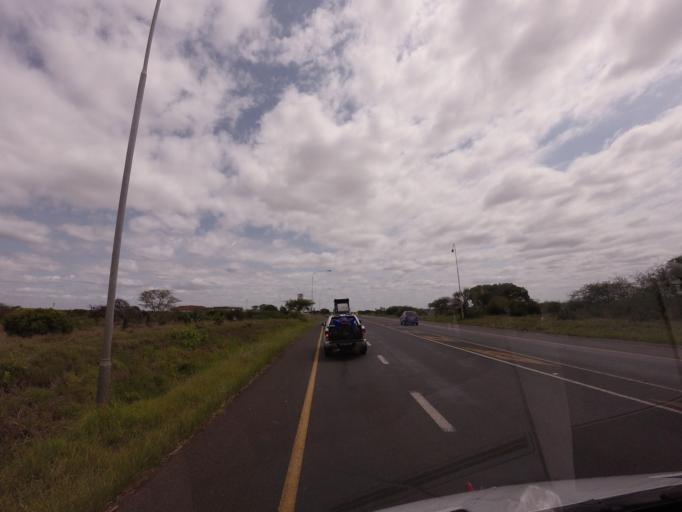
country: ZA
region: KwaZulu-Natal
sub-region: uMkhanyakude District Municipality
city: Hluhluwe
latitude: -28.0915
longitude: 32.2683
